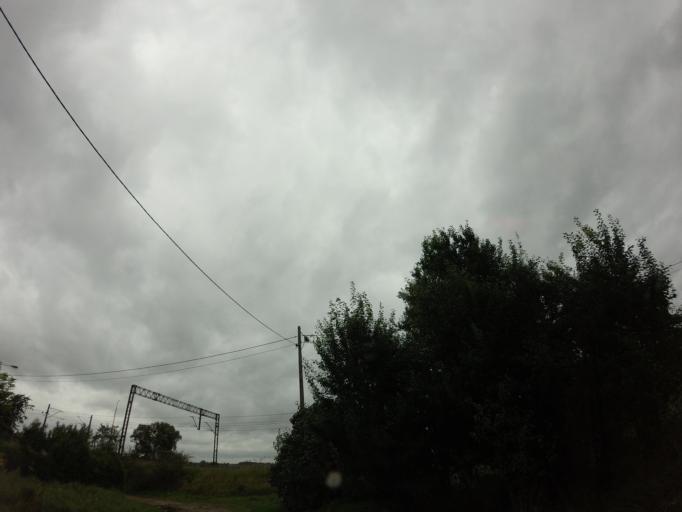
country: PL
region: West Pomeranian Voivodeship
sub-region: Powiat choszczenski
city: Choszczno
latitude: 53.1673
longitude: 15.3981
